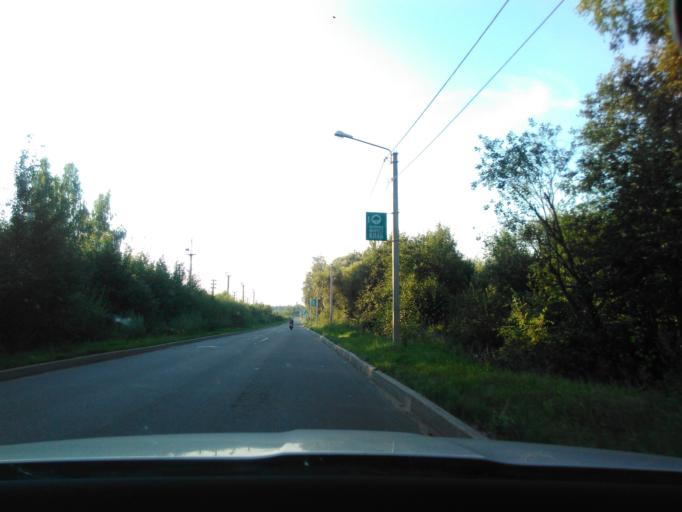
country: RU
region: Tverskaya
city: Konakovo
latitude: 56.7329
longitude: 36.7838
